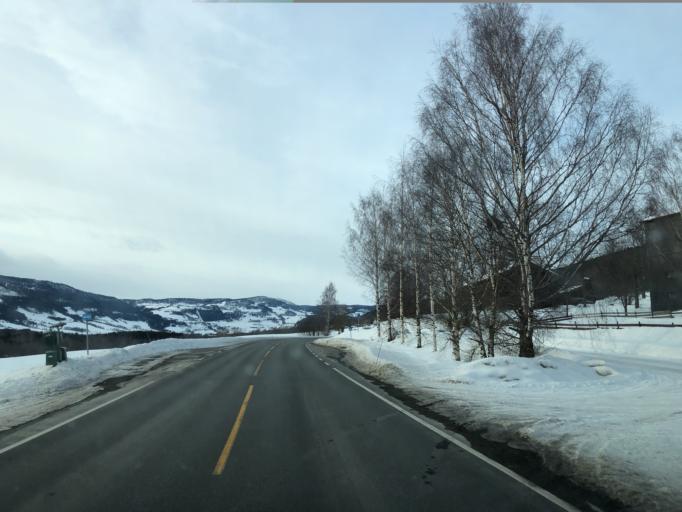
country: NO
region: Oppland
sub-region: Gausdal
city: Segalstad bru
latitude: 61.2395
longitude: 10.2012
